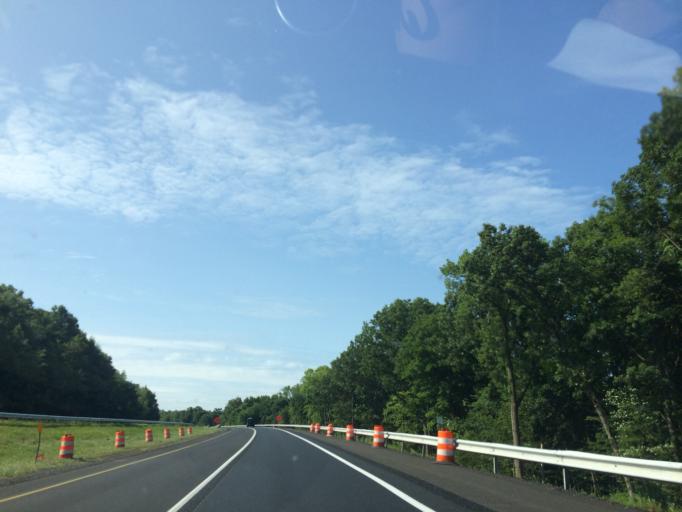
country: US
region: New York
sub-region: Ulster County
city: Clintondale
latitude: 41.6787
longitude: -74.0805
